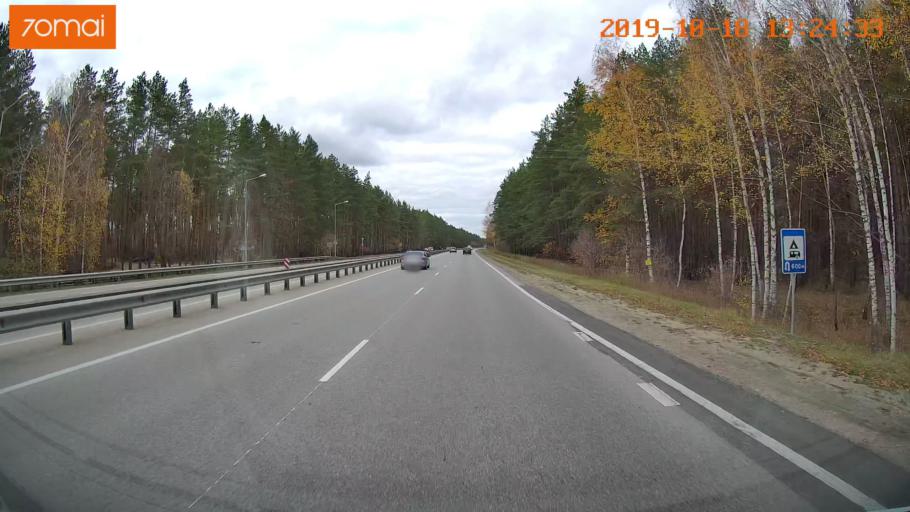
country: RU
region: Rjazan
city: Polyany
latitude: 54.7323
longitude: 39.8432
